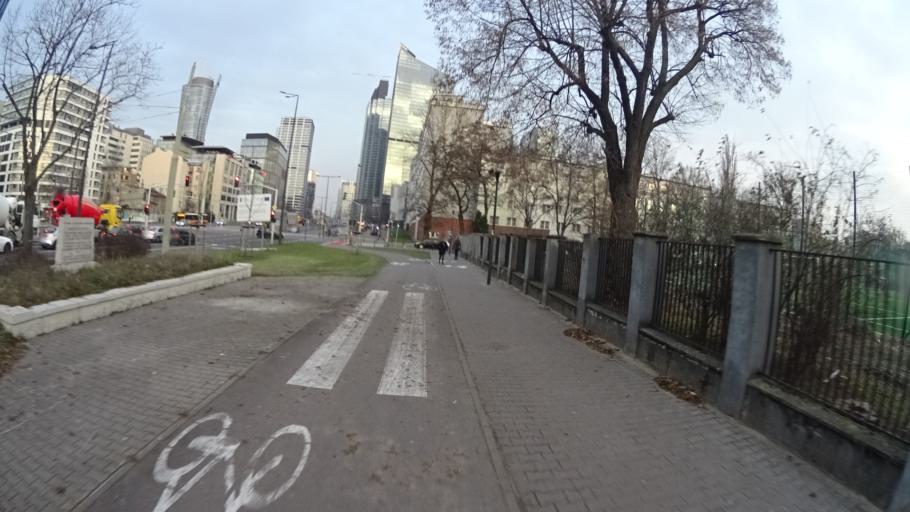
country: PL
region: Masovian Voivodeship
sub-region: Warszawa
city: Ochota
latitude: 52.2286
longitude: 20.9777
